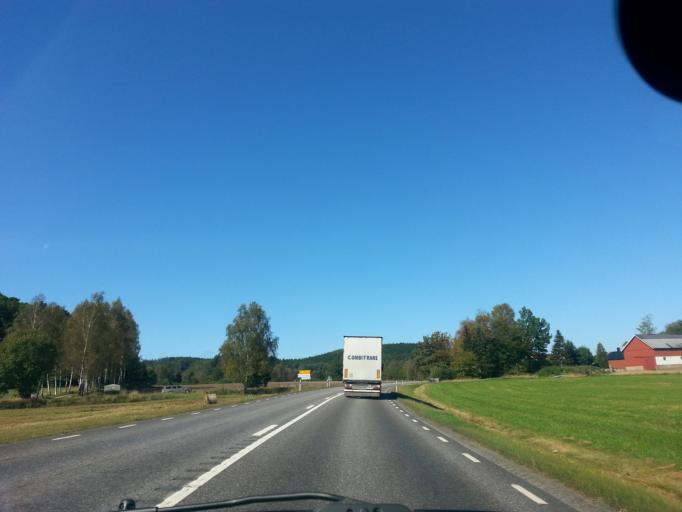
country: SE
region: Vaestra Goetaland
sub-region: Harryda Kommun
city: Ravlanda
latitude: 57.5878
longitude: 12.4565
